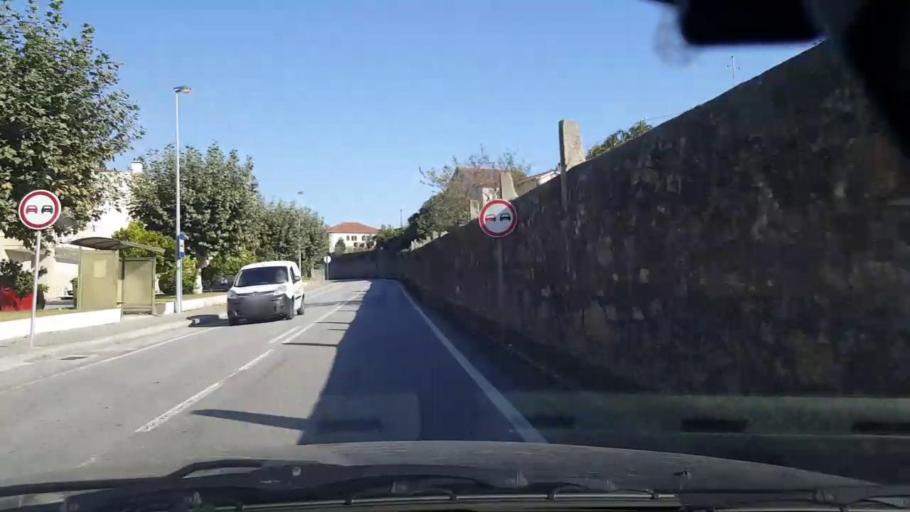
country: PT
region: Porto
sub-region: Vila do Conde
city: Arvore
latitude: 41.3340
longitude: -8.6687
